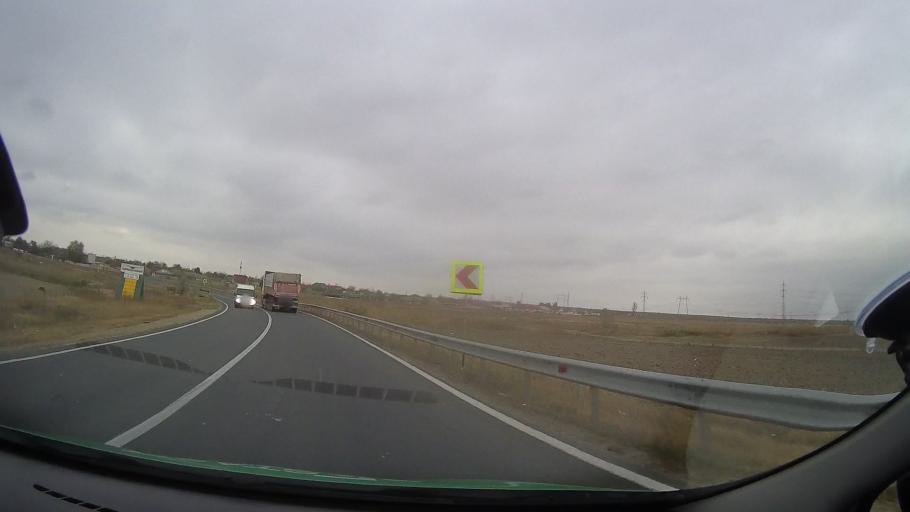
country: RO
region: Constanta
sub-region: Comuna Castelu
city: Castelu
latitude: 44.2590
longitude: 28.3476
